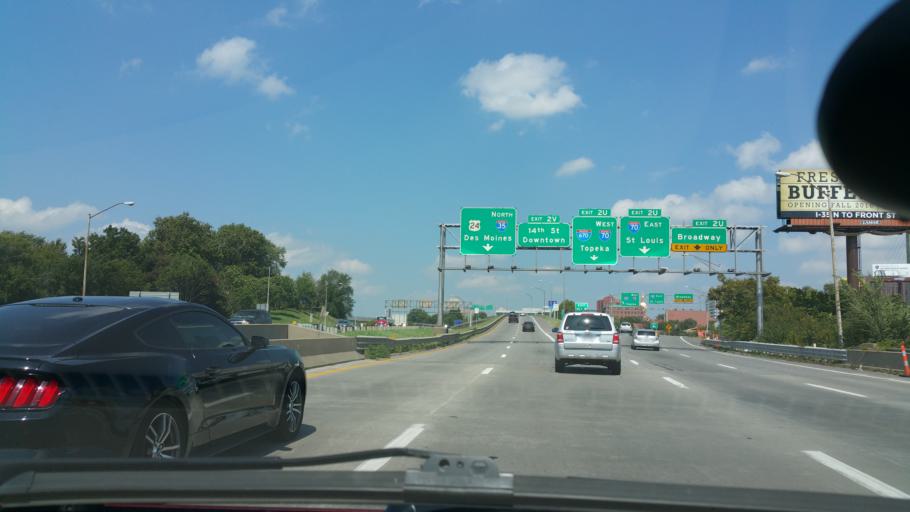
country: US
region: Missouri
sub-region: Jackson County
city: Kansas City
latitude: 39.0927
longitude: -94.5908
